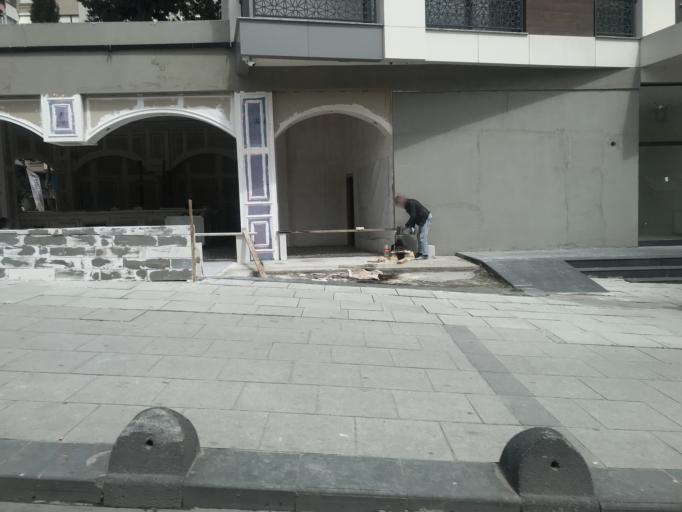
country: TR
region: Istanbul
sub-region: Atasehir
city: Atasehir
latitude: 40.9581
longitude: 29.0958
